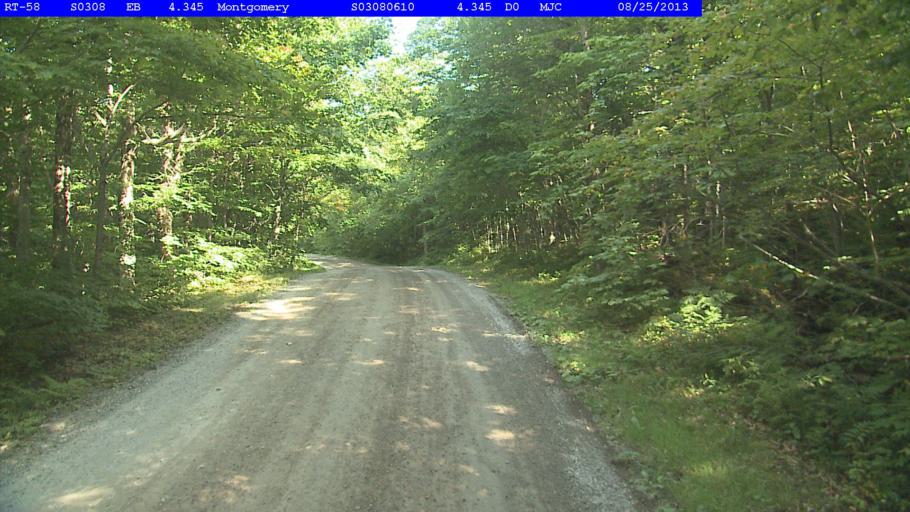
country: US
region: Vermont
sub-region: Franklin County
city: Richford
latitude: 44.8443
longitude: -72.5408
